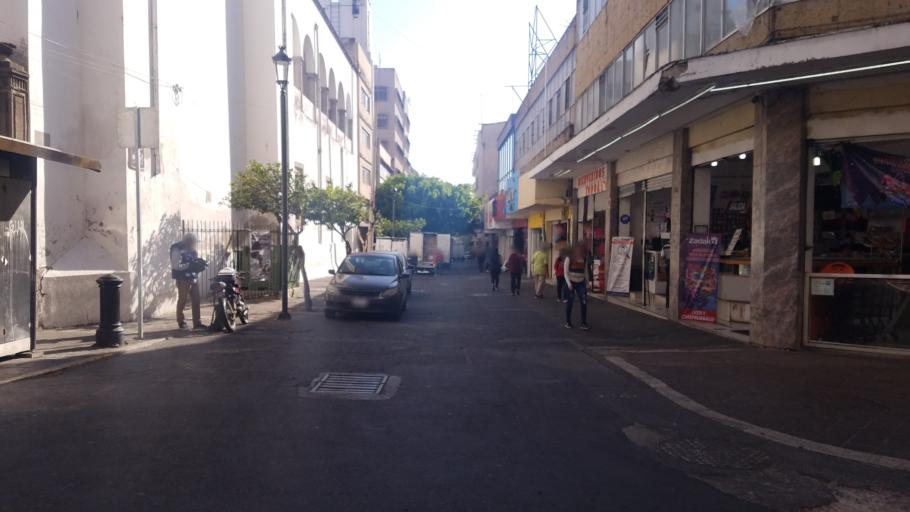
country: MX
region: Jalisco
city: Guadalajara
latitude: 20.6759
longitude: -103.3450
